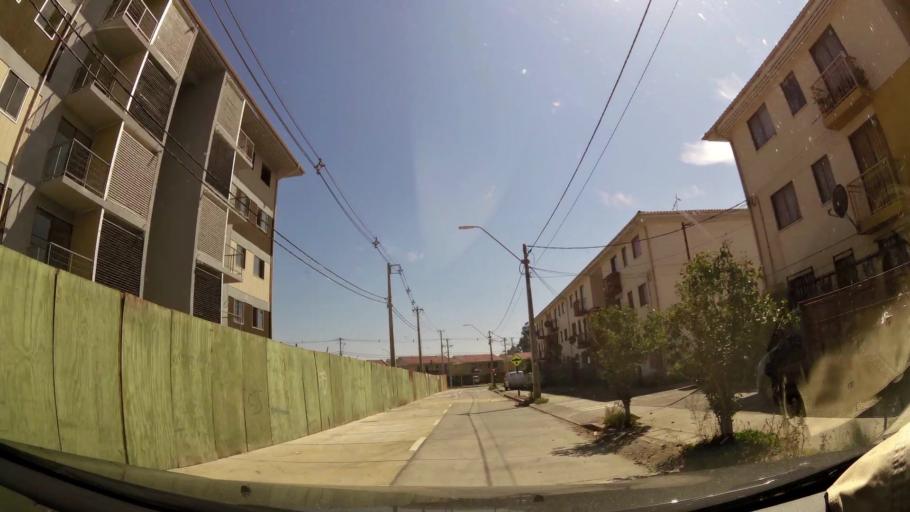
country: CL
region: Santiago Metropolitan
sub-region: Provincia de Santiago
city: Lo Prado
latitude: -33.3937
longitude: -70.7523
